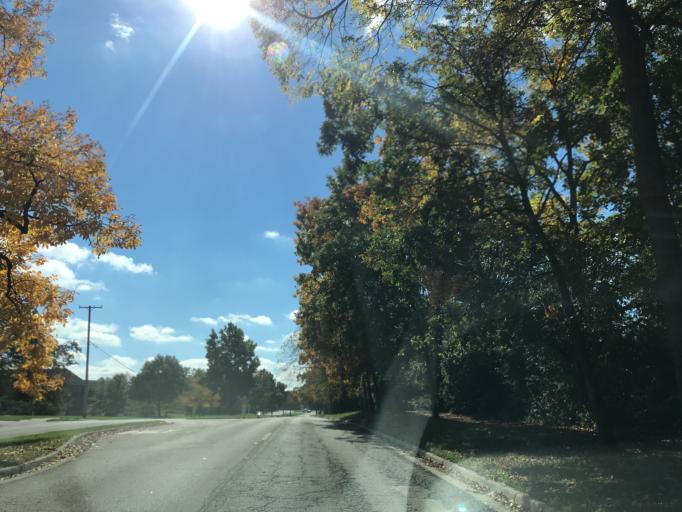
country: US
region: Michigan
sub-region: Washtenaw County
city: Ann Arbor
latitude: 42.2911
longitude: -83.6825
